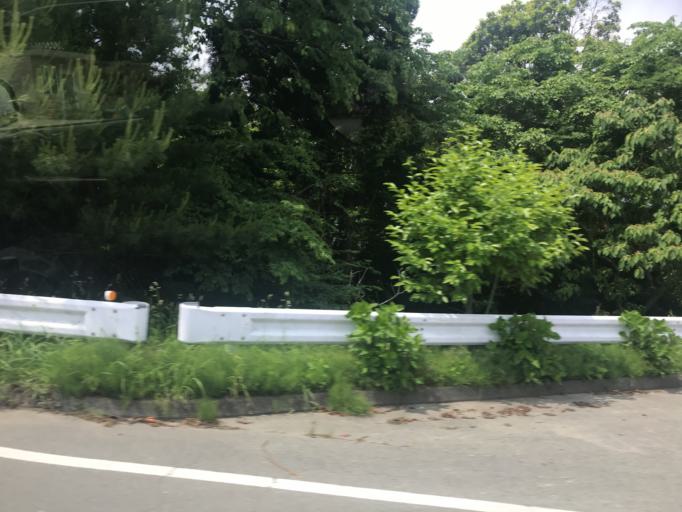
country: JP
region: Fukushima
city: Namie
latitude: 37.2759
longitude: 141.0063
